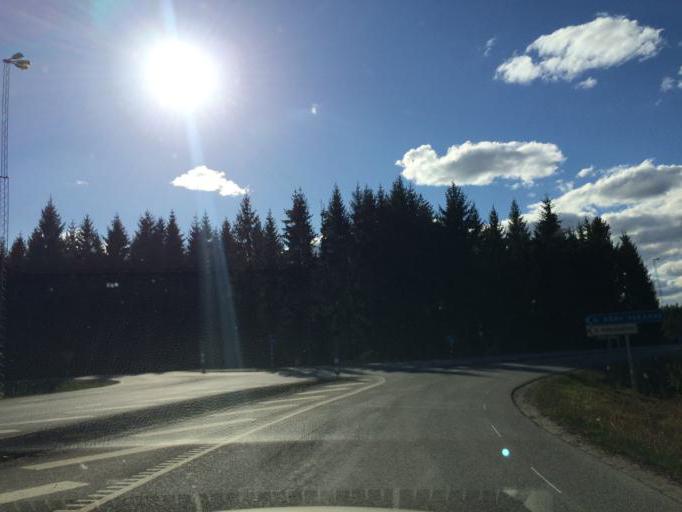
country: SE
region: Soedermanland
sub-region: Eskilstuna Kommun
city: Hallbybrunn
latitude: 59.4052
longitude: 16.3784
